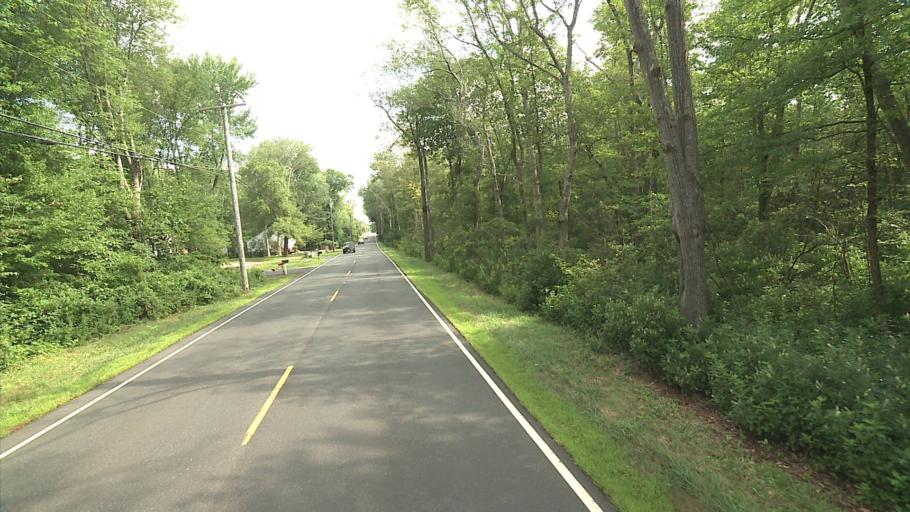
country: US
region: Connecticut
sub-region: Middlesex County
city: Moodus
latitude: 41.5291
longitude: -72.4126
